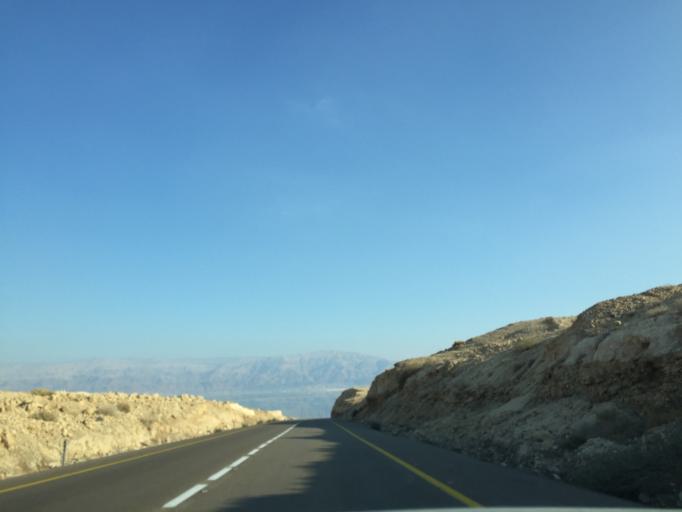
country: IL
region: Southern District
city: `En Boqeq
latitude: 31.1595
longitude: 35.3304
